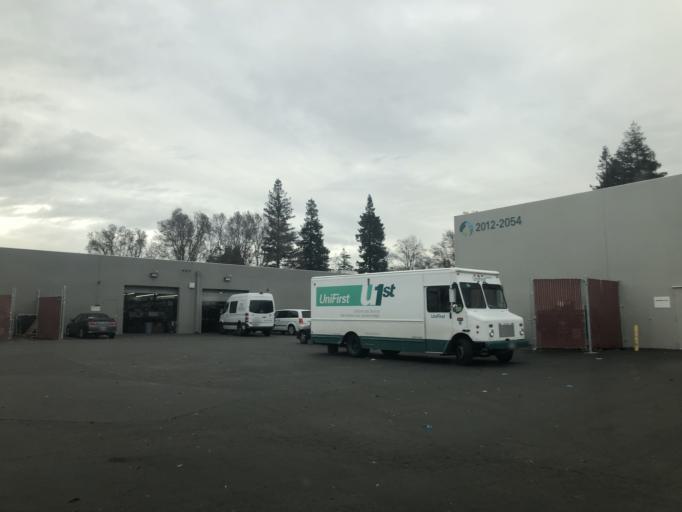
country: US
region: California
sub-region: Santa Clara County
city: San Jose
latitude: 37.3789
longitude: -121.9131
